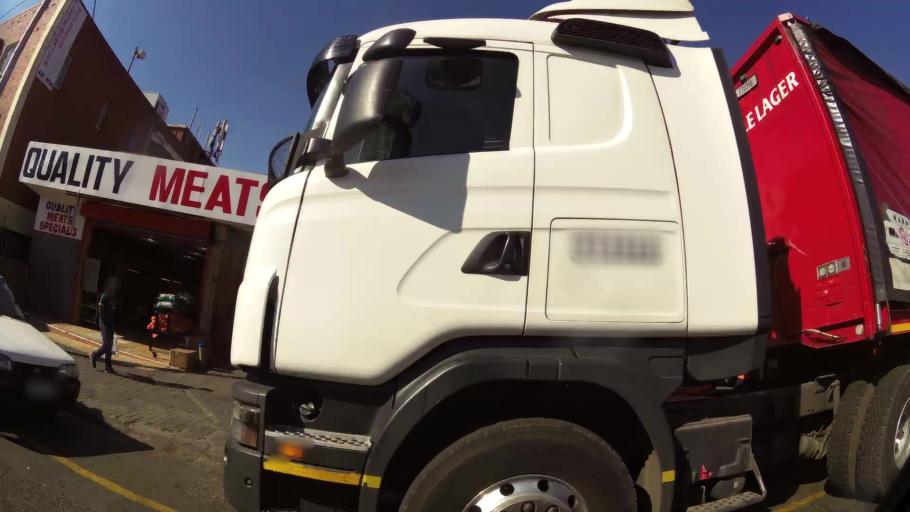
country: ZA
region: Gauteng
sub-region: City of Johannesburg Metropolitan Municipality
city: Johannesburg
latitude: -26.2485
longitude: 28.0521
